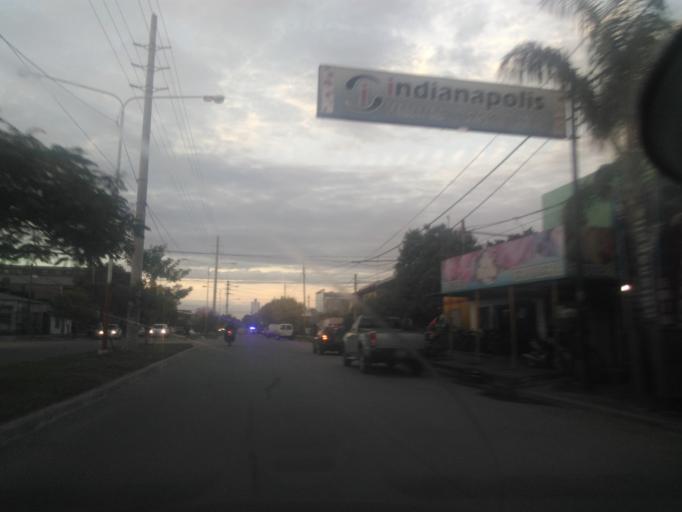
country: AR
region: Chaco
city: Resistencia
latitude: -27.4690
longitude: -58.9976
